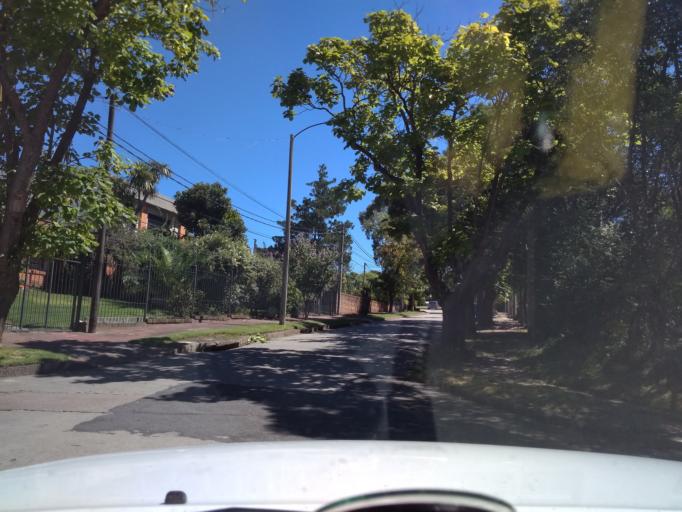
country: UY
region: Canelones
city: Paso de Carrasco
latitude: -34.8894
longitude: -56.0738
